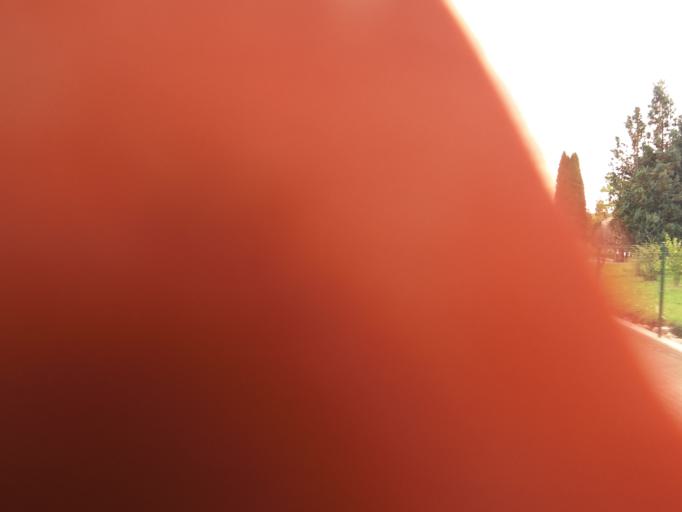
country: DE
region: Saxony-Anhalt
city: Kretzschau
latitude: 51.0643
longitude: 12.0589
